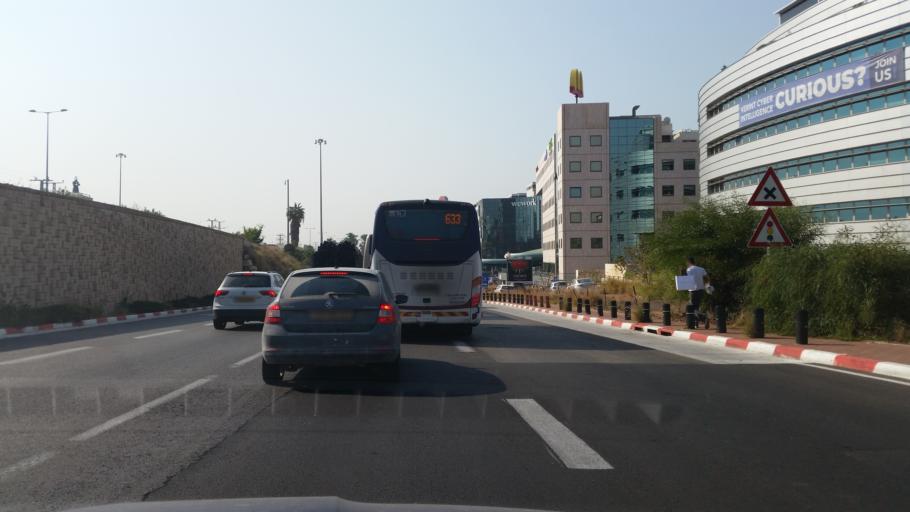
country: IL
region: Tel Aviv
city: Herzliyya
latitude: 32.1621
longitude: 34.8117
